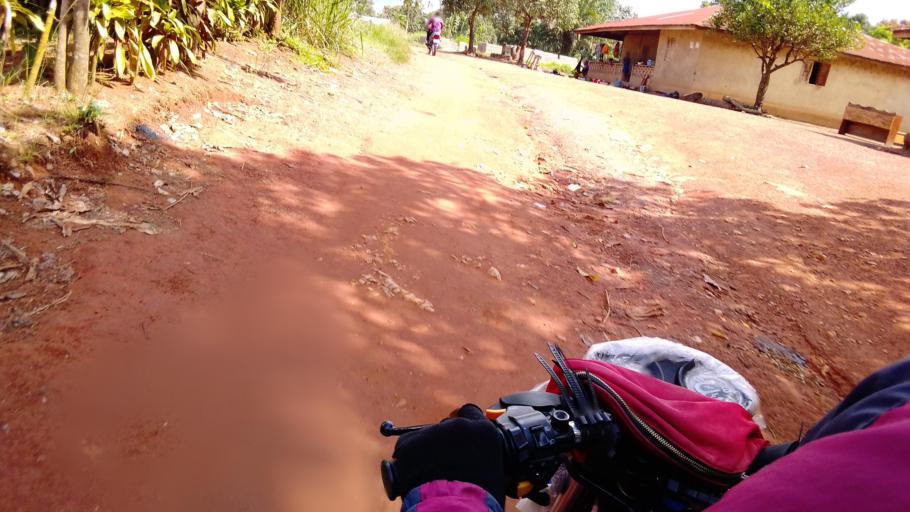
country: SL
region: Eastern Province
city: Koidu
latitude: 8.6622
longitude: -10.9785
